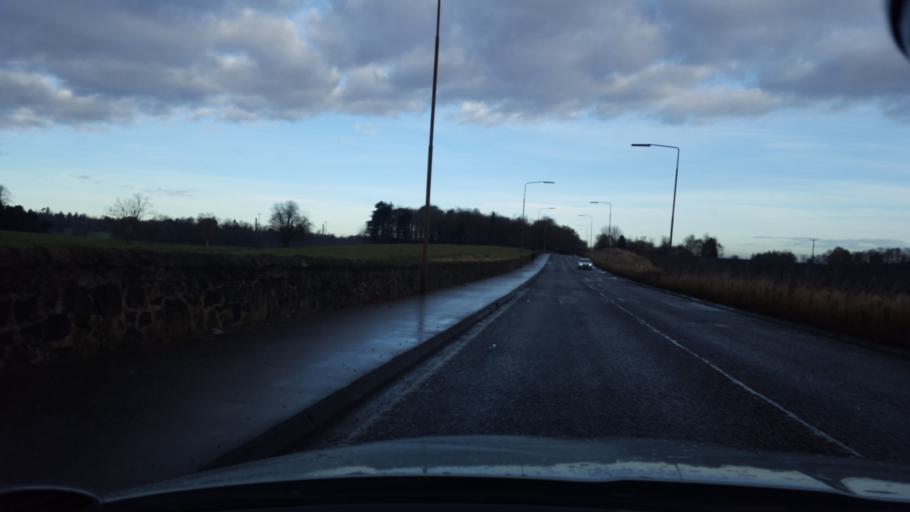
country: GB
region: Scotland
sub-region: Edinburgh
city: Kirkliston
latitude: 55.9691
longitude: -3.4011
